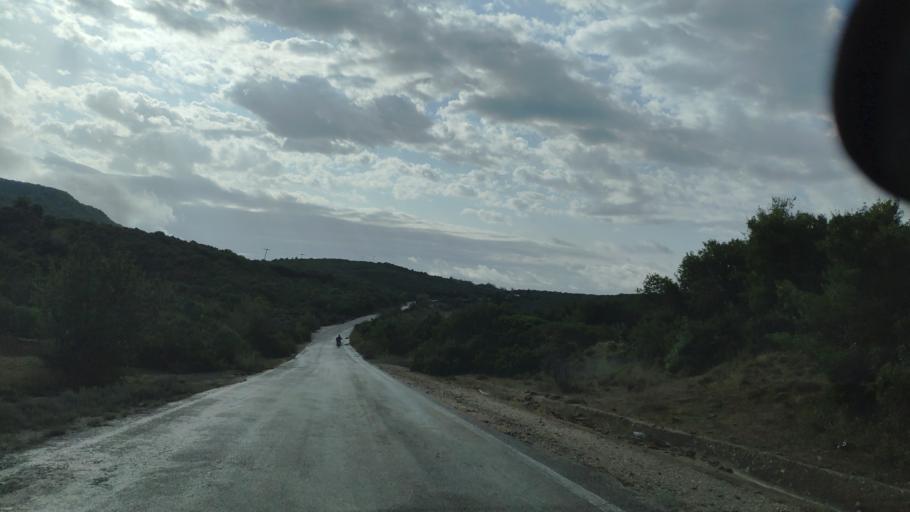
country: GR
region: West Greece
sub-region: Nomos Aitolias kai Akarnanias
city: Sardinia
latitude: 38.8846
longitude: 21.2437
